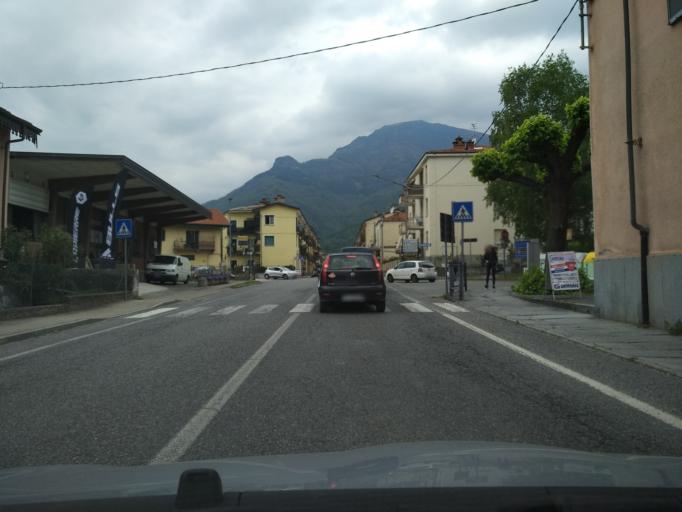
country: IT
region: Piedmont
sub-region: Provincia di Torino
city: Torre Pellice
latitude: 44.8203
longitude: 7.2307
